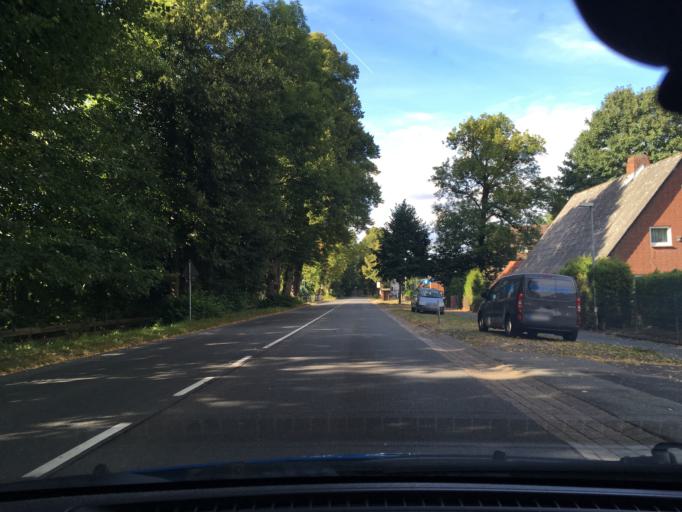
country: DE
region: Lower Saxony
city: Seevetal
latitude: 53.4045
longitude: 9.9249
